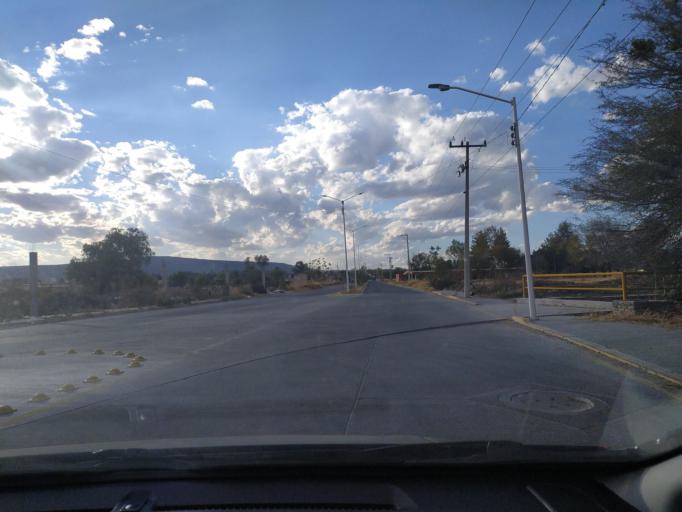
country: LA
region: Oudomxai
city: Muang La
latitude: 21.0163
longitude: 101.8296
